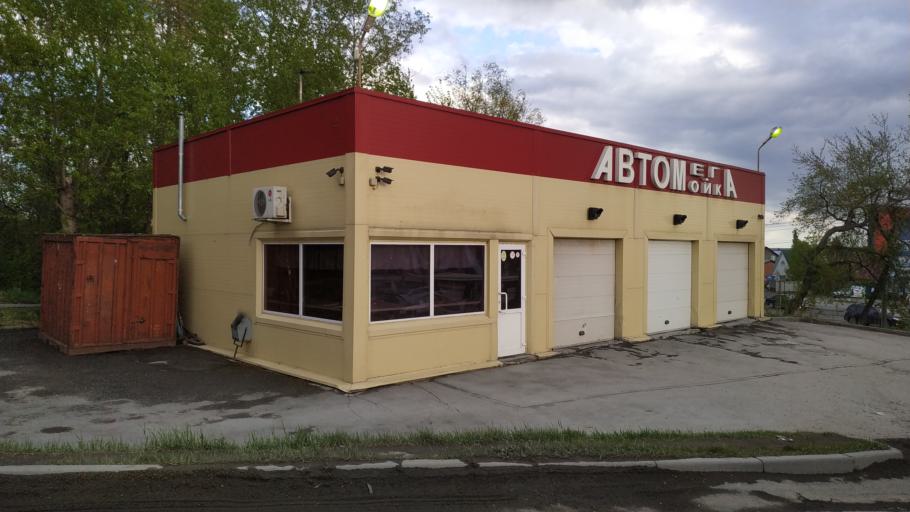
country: RU
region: Novosibirsk
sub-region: Novosibirskiy Rayon
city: Novosibirsk
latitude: 54.9922
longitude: 82.9806
